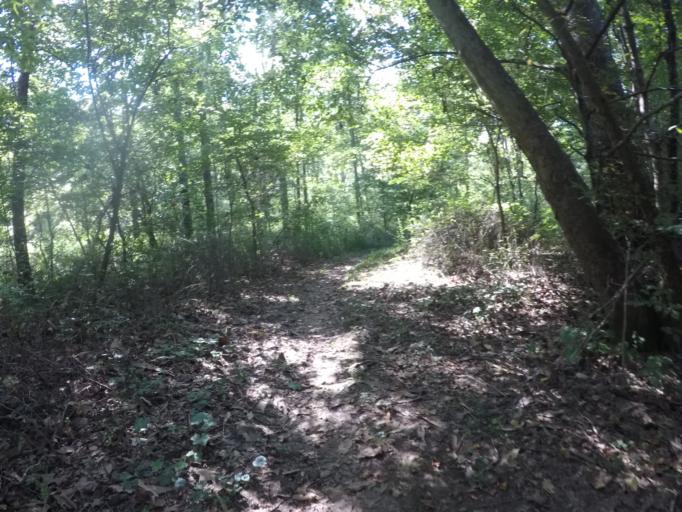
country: US
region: Ohio
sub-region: Lawrence County
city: Ironton
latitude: 38.6310
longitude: -82.6077
